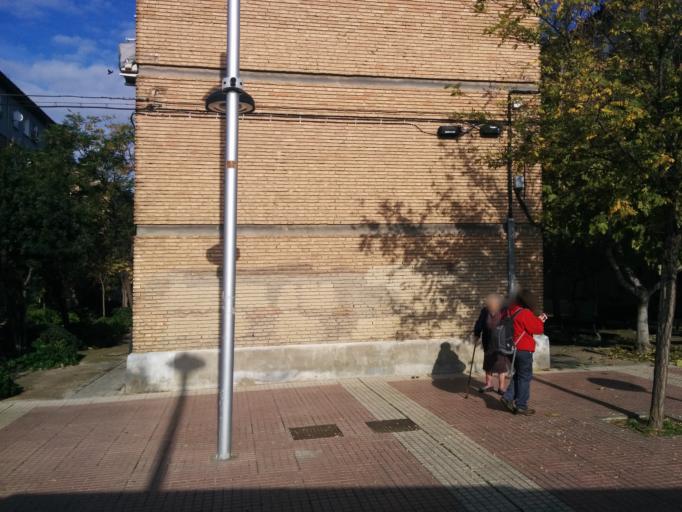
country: ES
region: Aragon
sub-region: Provincia de Zaragoza
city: Zaragoza
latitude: 41.6281
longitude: -0.8868
